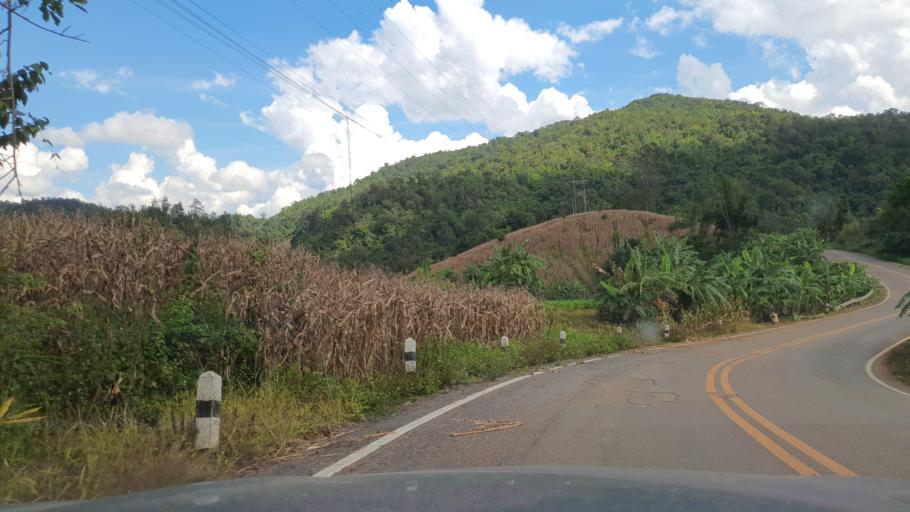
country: TH
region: Chiang Rai
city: Wiang Pa Pao
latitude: 19.3096
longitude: 99.4171
